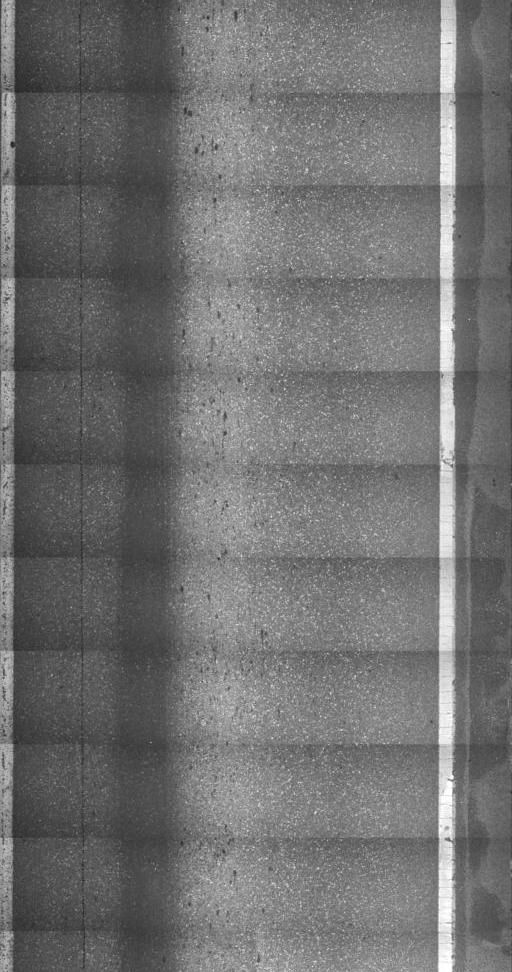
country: US
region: New Hampshire
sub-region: Grafton County
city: Haverhill
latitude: 43.9821
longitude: -72.1209
